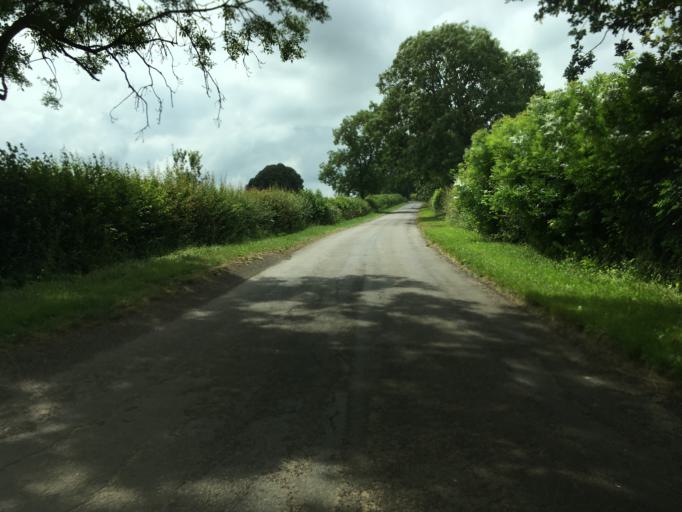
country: GB
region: England
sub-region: Oxfordshire
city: Bloxham
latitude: 51.9633
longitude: -1.3892
